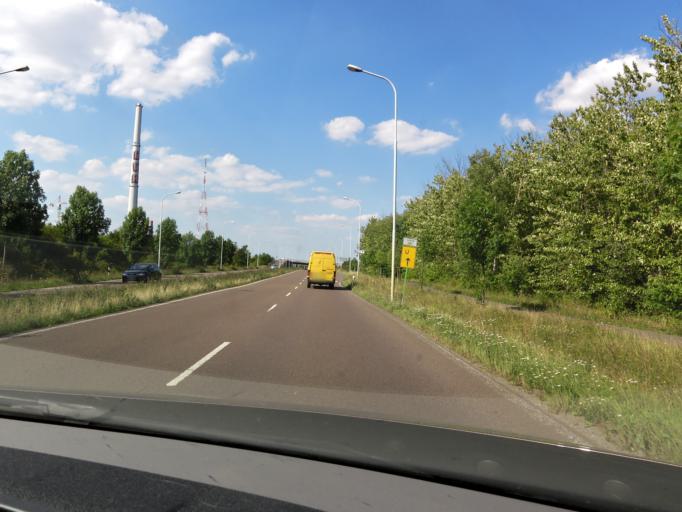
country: DE
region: Saxony-Anhalt
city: Halle (Saale)
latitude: 51.4543
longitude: 11.9957
